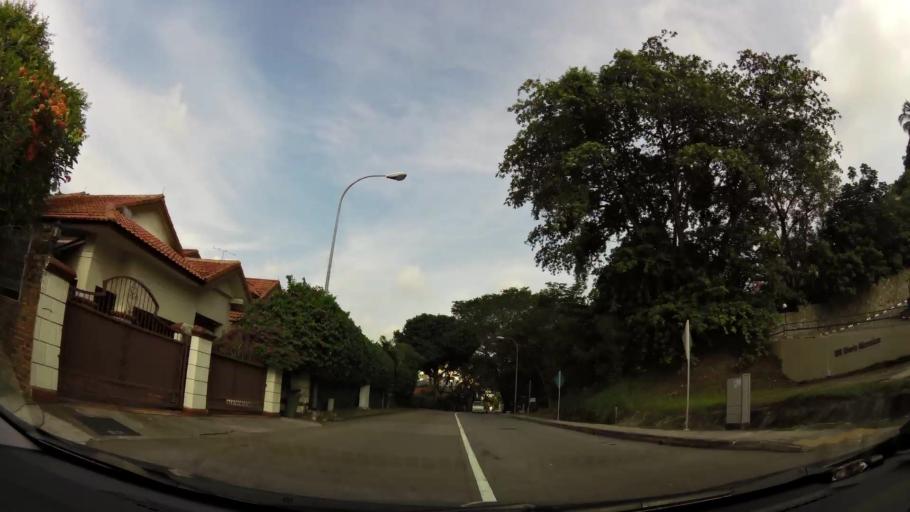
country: SG
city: Singapore
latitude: 1.2864
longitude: 103.7798
